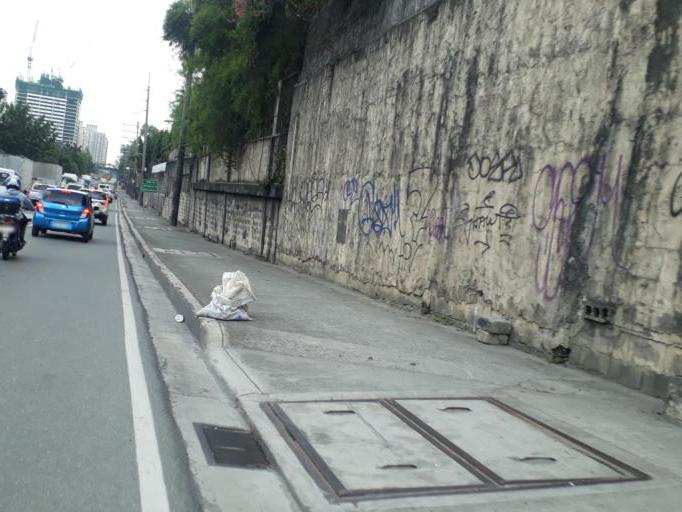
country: PH
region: Metro Manila
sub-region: Pasig
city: Pasig City
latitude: 14.5997
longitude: 121.0793
